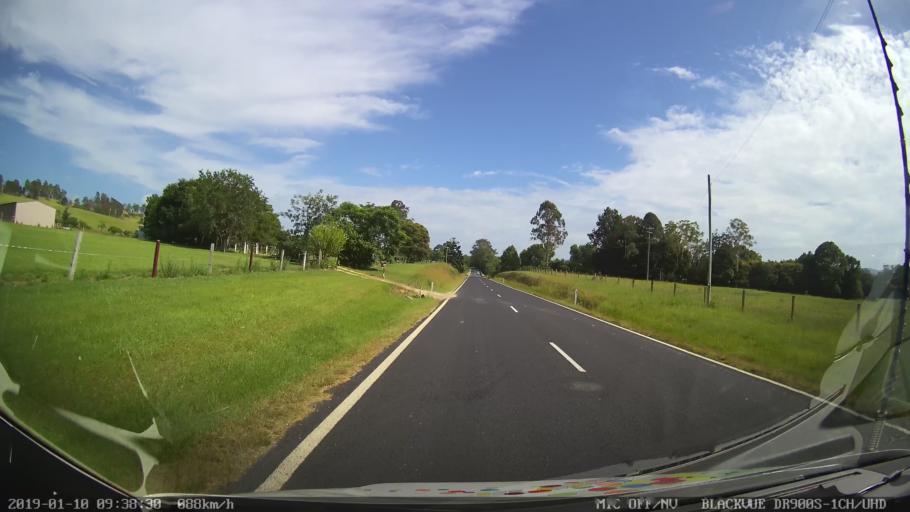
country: AU
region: New South Wales
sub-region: Coffs Harbour
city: Nana Glen
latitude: -30.1757
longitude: 153.0068
